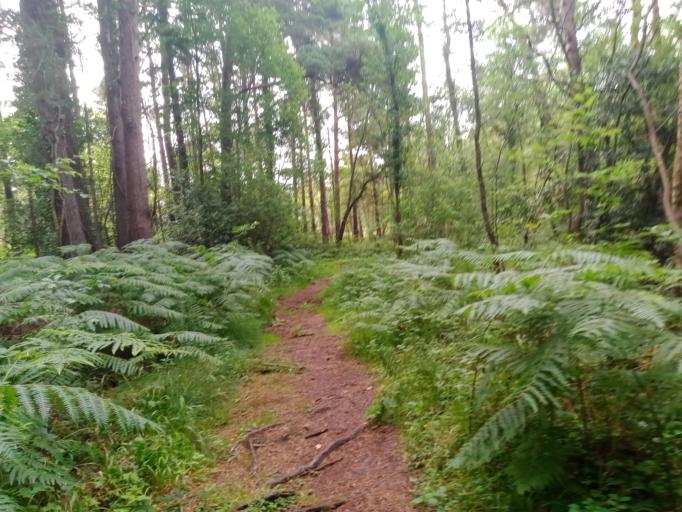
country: IE
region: Leinster
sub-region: Laois
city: Abbeyleix
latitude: 52.8843
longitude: -7.3569
